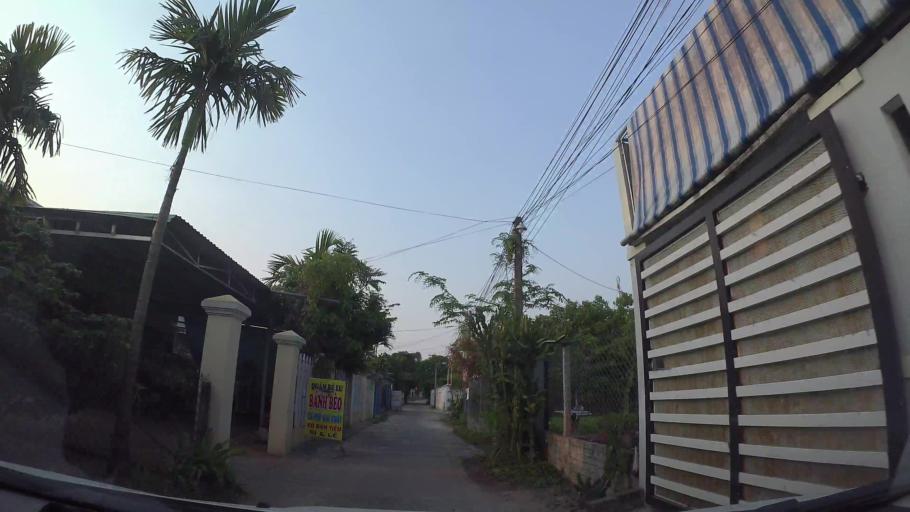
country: VN
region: Da Nang
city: Ngu Hanh Son
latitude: 15.9539
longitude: 108.2536
